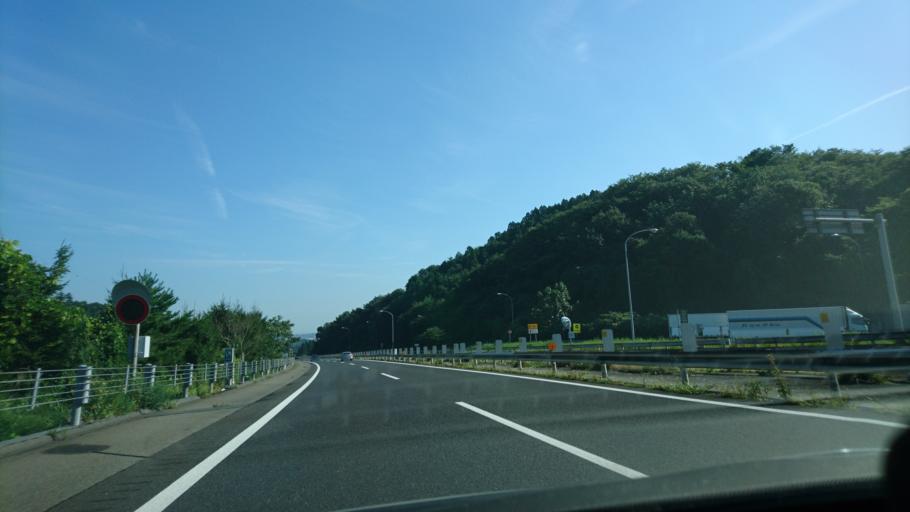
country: JP
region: Iwate
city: Ichinoseki
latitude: 38.9633
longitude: 141.1113
